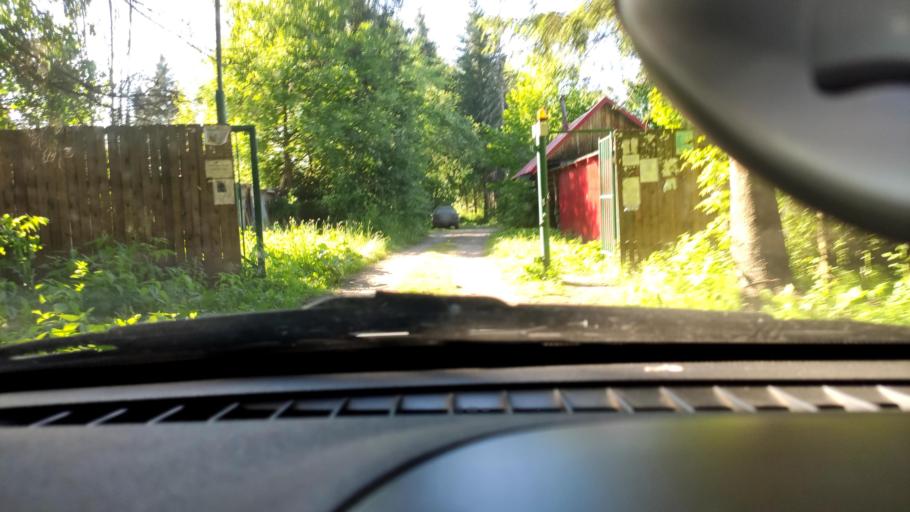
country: RU
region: Perm
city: Bershet'
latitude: 57.6999
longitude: 56.4070
